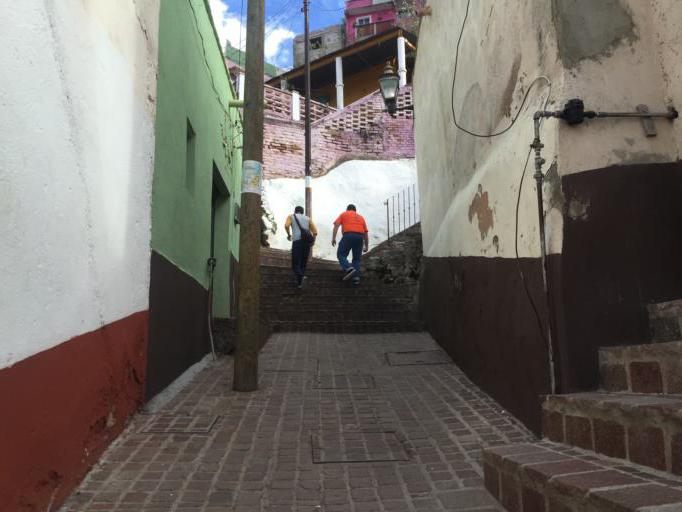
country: MX
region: Guanajuato
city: Guanajuato
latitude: 21.0153
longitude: -101.2559
